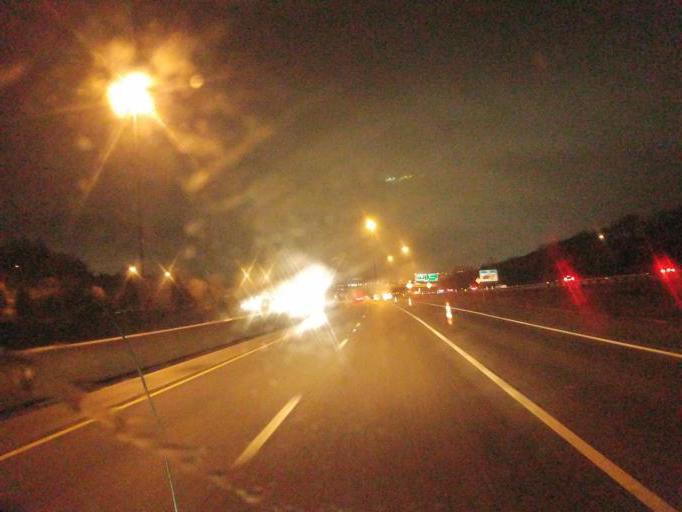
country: US
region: Missouri
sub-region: Saint Louis County
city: Sunset Hills
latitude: 38.5523
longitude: -90.4222
